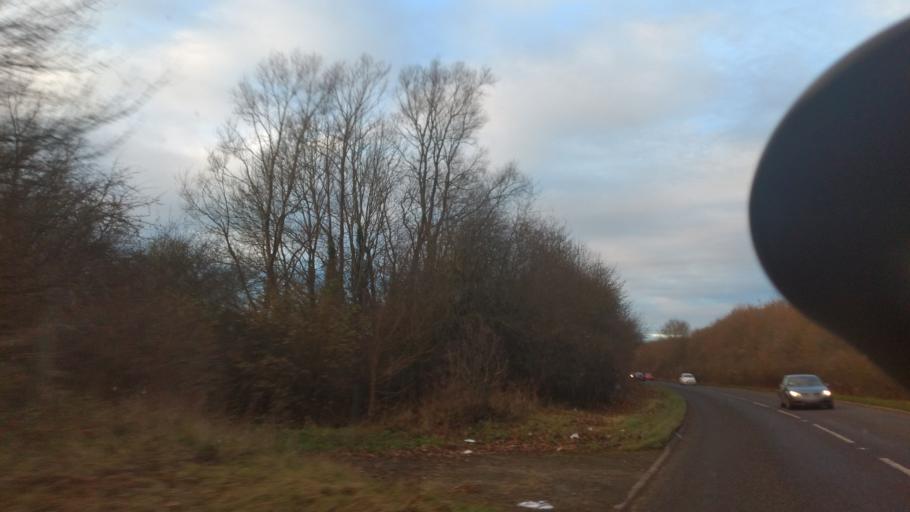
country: GB
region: England
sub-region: Somerset
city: Frome
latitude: 51.2545
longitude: -2.2939
